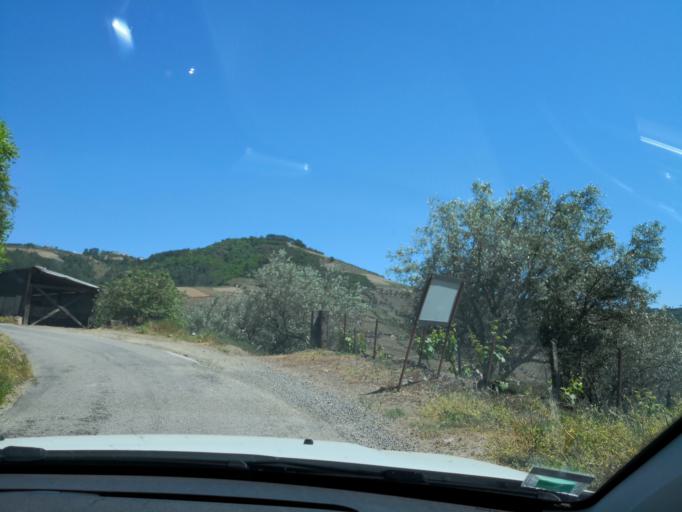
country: PT
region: Vila Real
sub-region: Vila Real
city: Vila Real
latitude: 41.2290
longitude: -7.7220
